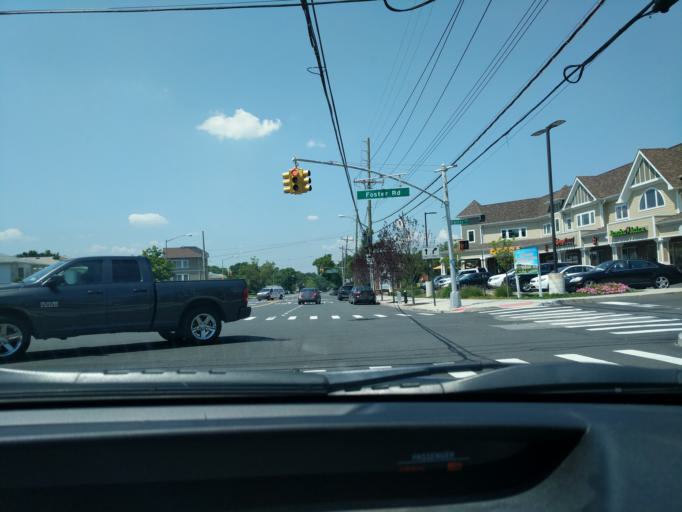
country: US
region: New Jersey
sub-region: Middlesex County
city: Carteret
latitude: 40.5419
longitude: -74.2069
